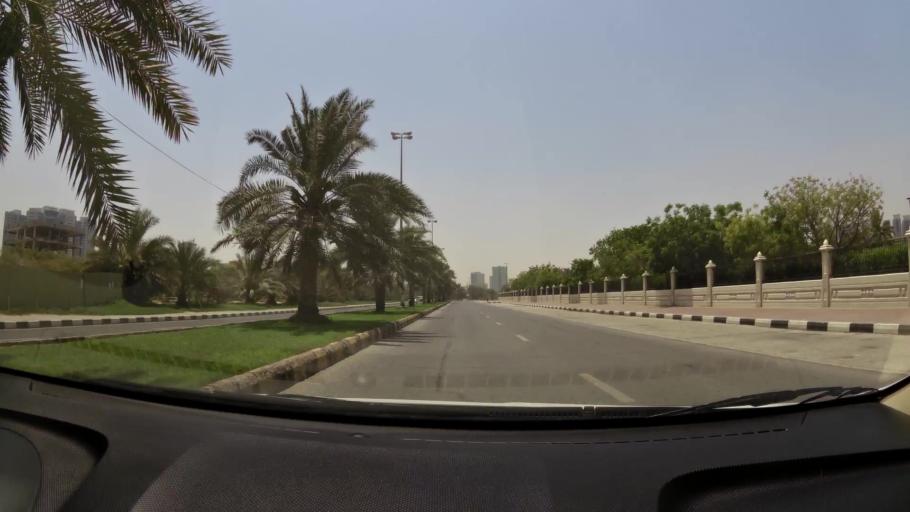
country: AE
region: Ajman
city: Ajman
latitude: 25.3981
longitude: 55.4429
